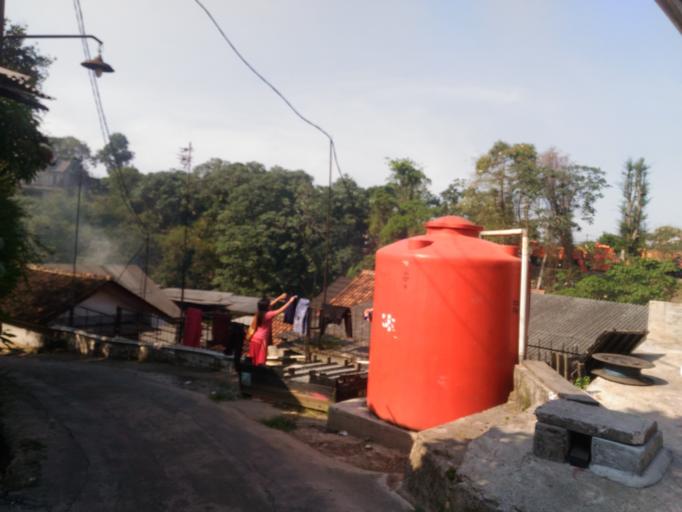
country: ID
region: West Java
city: Depok
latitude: -6.3421
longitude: 106.8384
